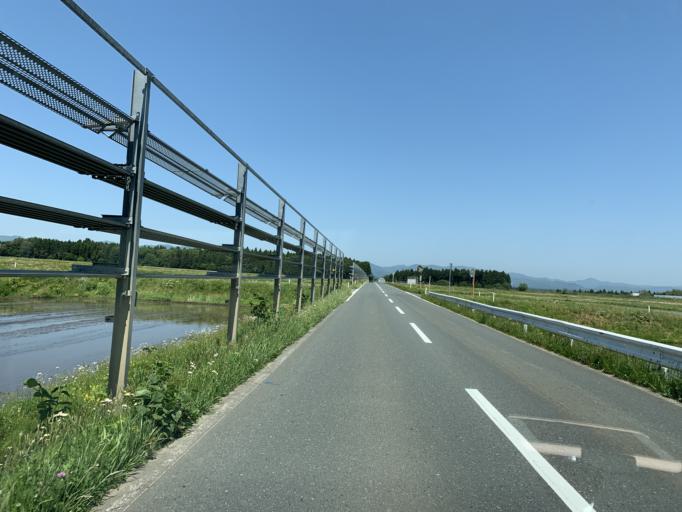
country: JP
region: Iwate
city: Kitakami
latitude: 39.2715
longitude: 141.0547
